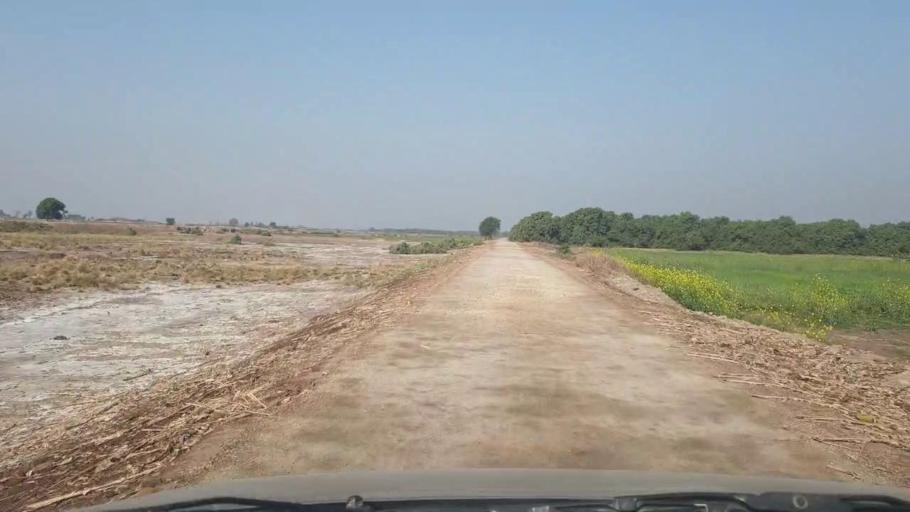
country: PK
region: Sindh
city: Mirwah Gorchani
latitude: 25.2522
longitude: 69.1022
